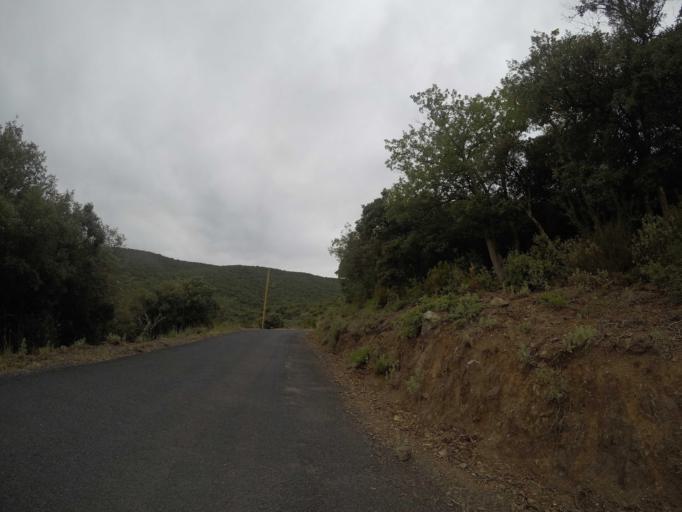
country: FR
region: Languedoc-Roussillon
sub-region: Departement des Pyrenees-Orientales
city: Ille-sur-Tet
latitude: 42.6330
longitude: 2.6157
